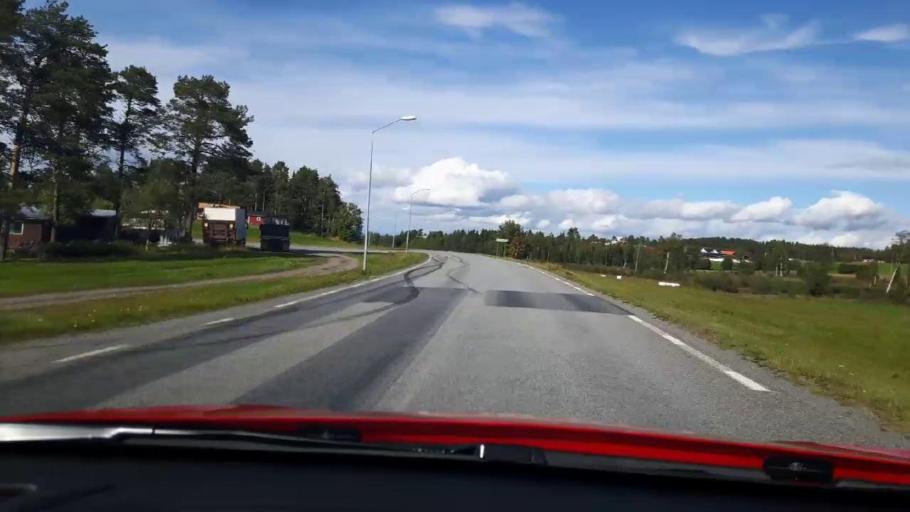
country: SE
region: Jaemtland
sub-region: OEstersunds Kommun
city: Ostersund
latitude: 63.0952
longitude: 14.4389
